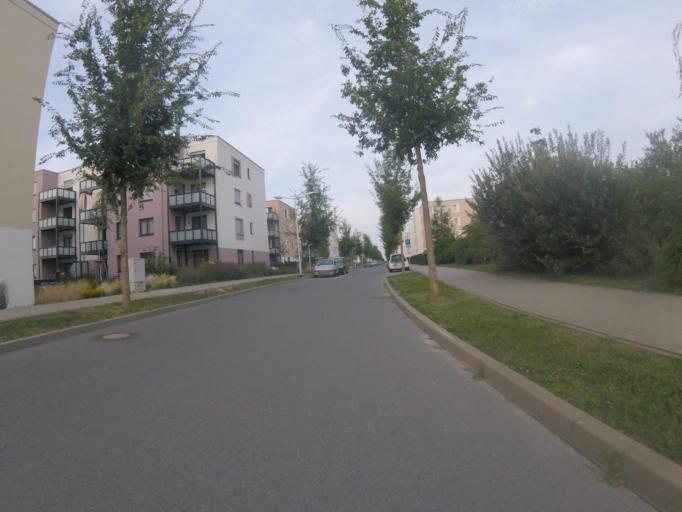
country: DE
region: Brandenburg
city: Schonefeld
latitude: 52.3948
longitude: 13.4951
